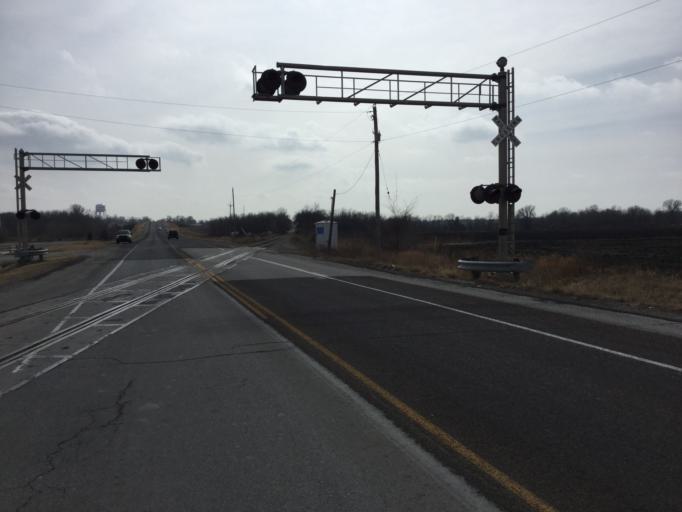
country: US
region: Kansas
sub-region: Franklin County
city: Ottawa
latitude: 38.6421
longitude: -95.2676
